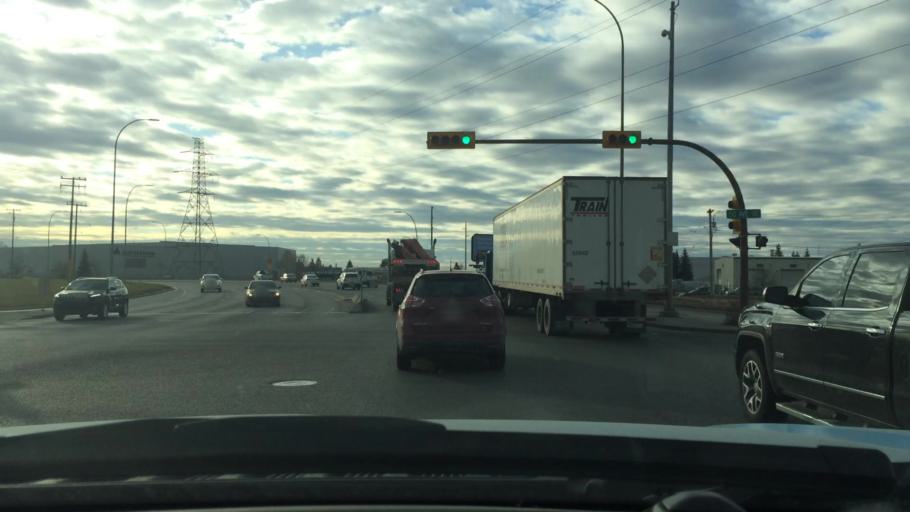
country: CA
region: Alberta
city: Calgary
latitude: 51.0088
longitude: -114.0019
